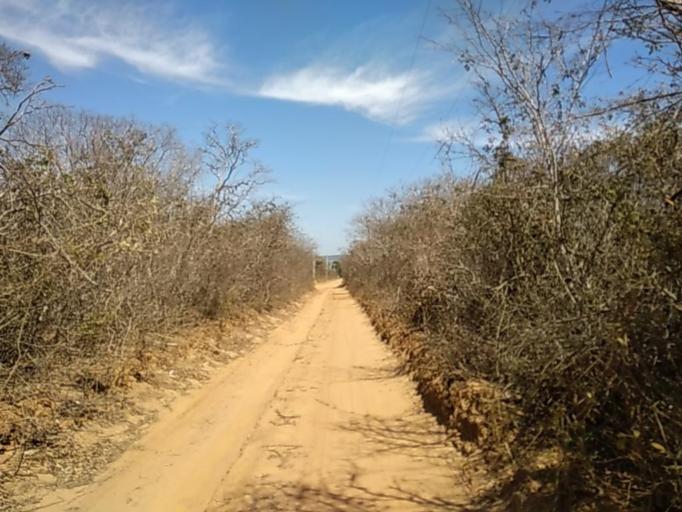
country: BR
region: Bahia
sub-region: Caetite
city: Caetite
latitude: -13.9782
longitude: -42.5118
